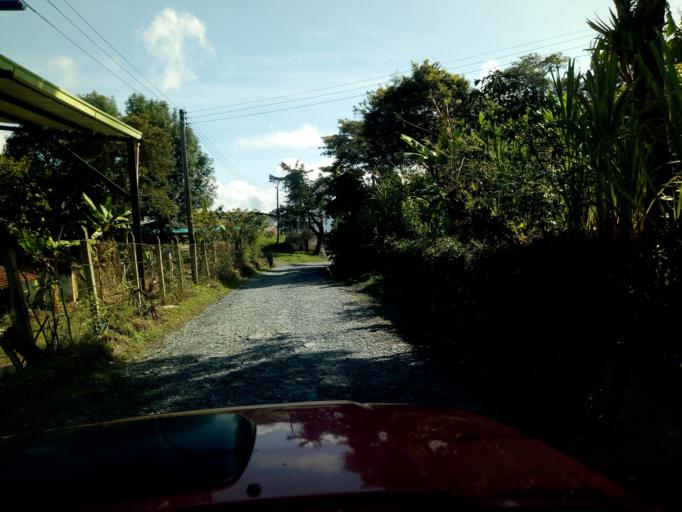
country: CO
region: Boyaca
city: Moniquira
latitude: 5.8846
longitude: -73.5444
